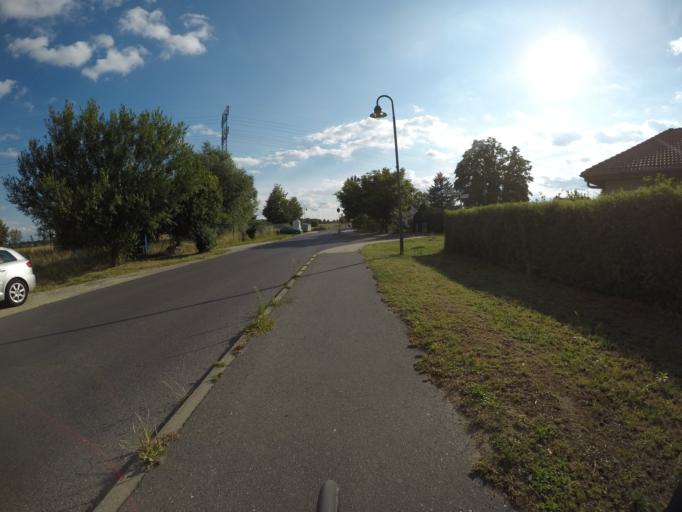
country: DE
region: Berlin
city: Falkenberg
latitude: 52.5897
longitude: 13.5426
